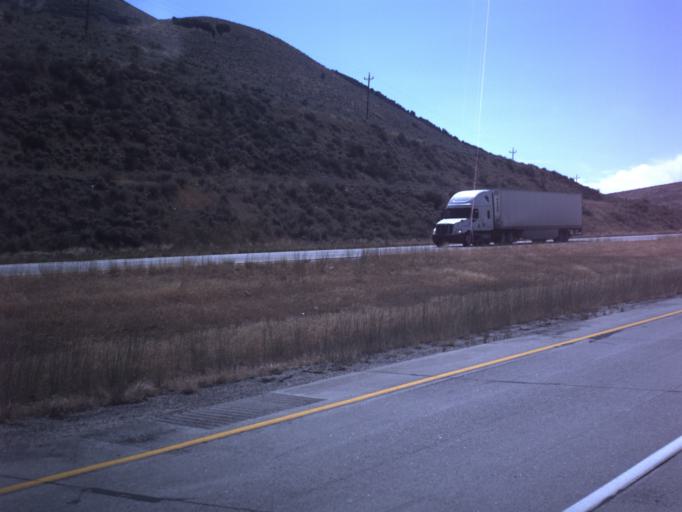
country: US
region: Utah
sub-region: Box Elder County
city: Garland
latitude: 41.8050
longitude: -112.3214
